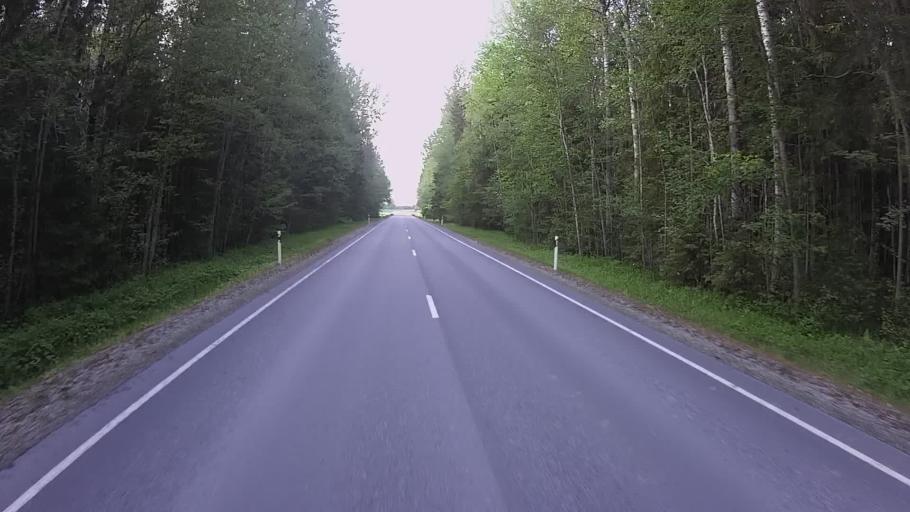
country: EE
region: Jogevamaa
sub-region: Mustvee linn
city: Mustvee
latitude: 58.8828
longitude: 26.8150
